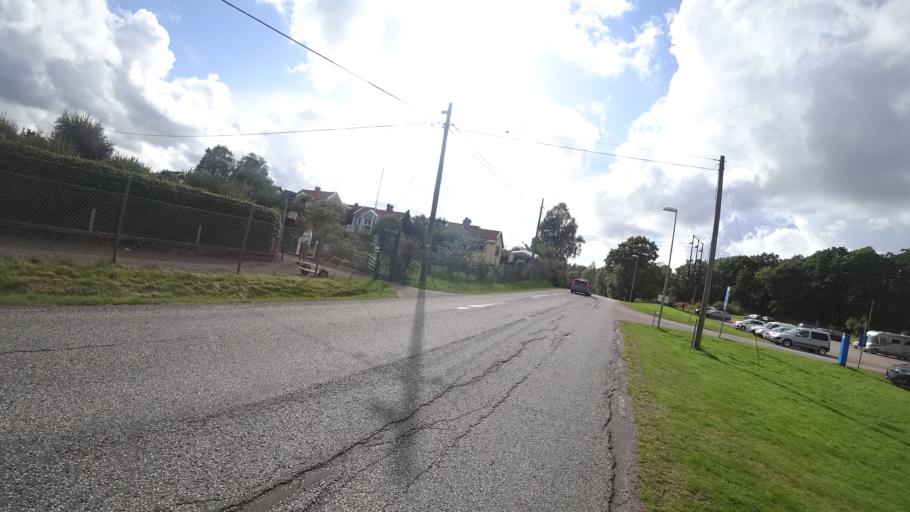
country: SE
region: Vaestra Goetaland
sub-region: Molndal
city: Moelndal
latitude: 57.6983
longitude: 12.0373
